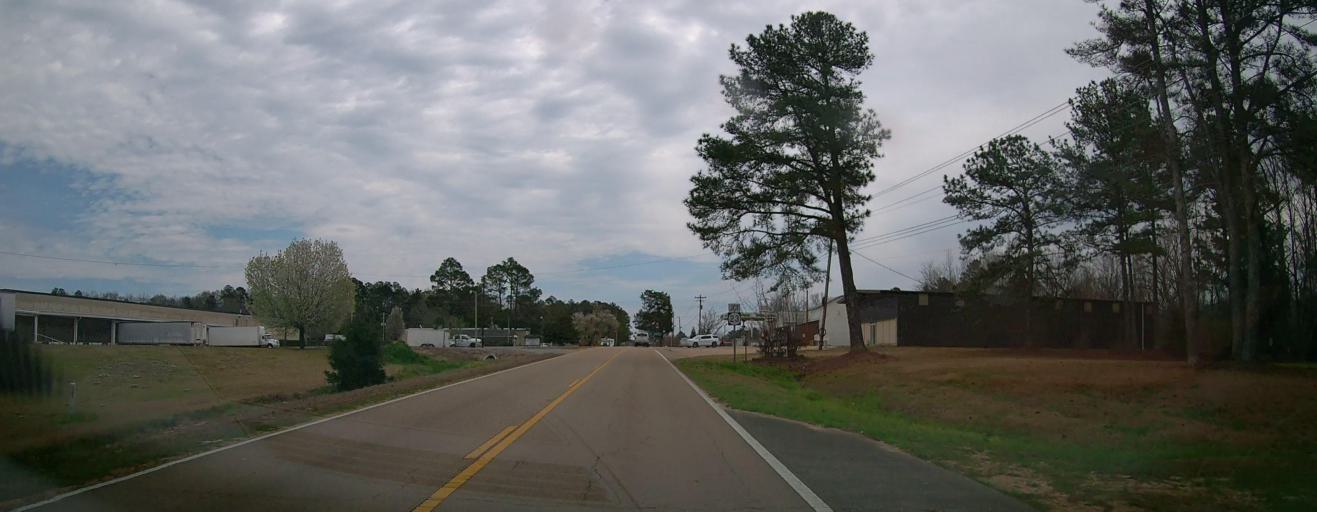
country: US
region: Mississippi
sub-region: Itawamba County
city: Fulton
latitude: 34.2372
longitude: -88.2662
